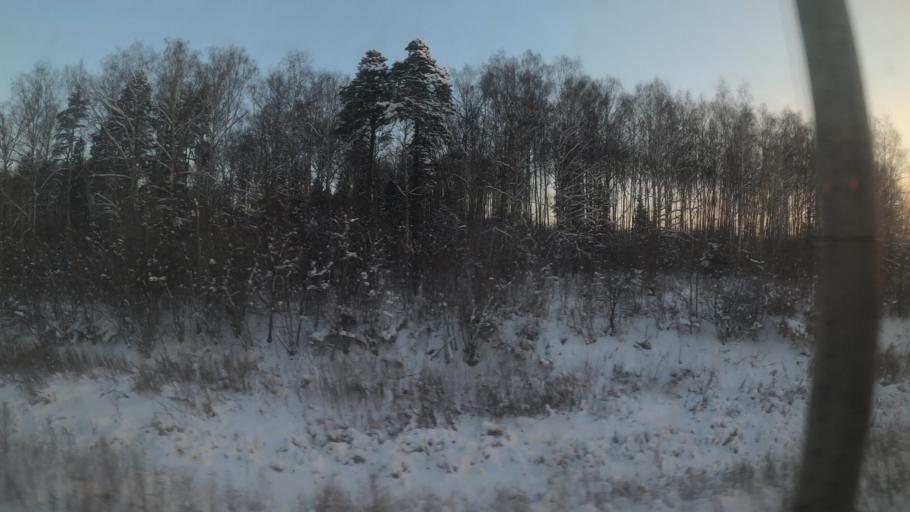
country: RU
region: Moskovskaya
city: Dedenevo
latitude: 56.2293
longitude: 37.5217
